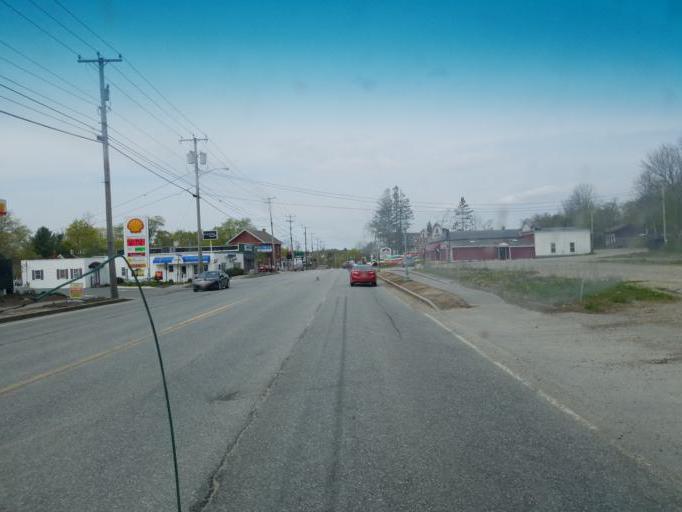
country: US
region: Maine
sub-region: Hancock County
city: Ellsworth
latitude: 44.5407
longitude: -68.4174
